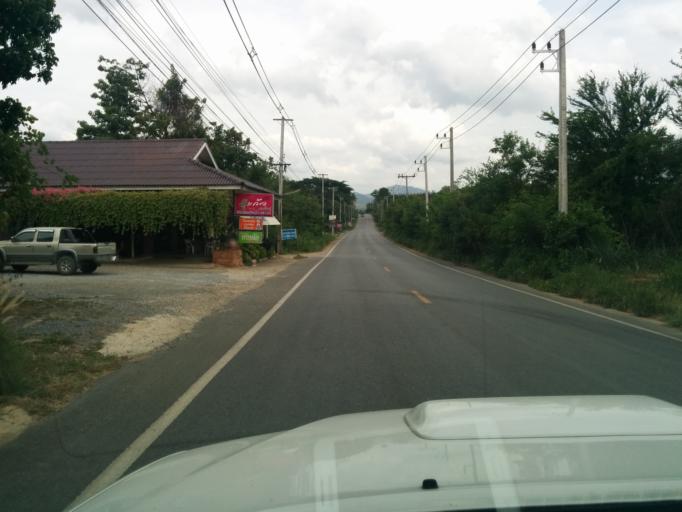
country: TH
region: Sara Buri
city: Muak Lek
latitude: 14.6149
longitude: 101.2123
